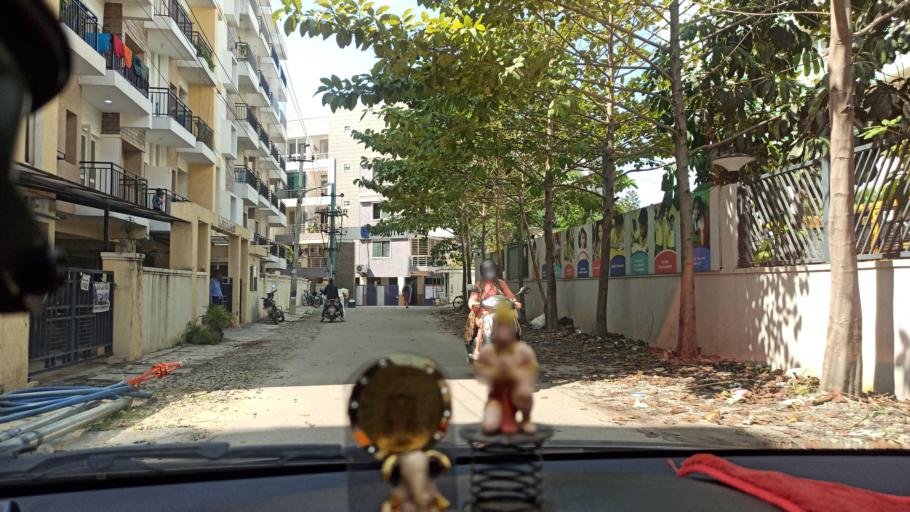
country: IN
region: Karnataka
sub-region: Bangalore Urban
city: Bangalore
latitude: 12.9777
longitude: 77.6921
